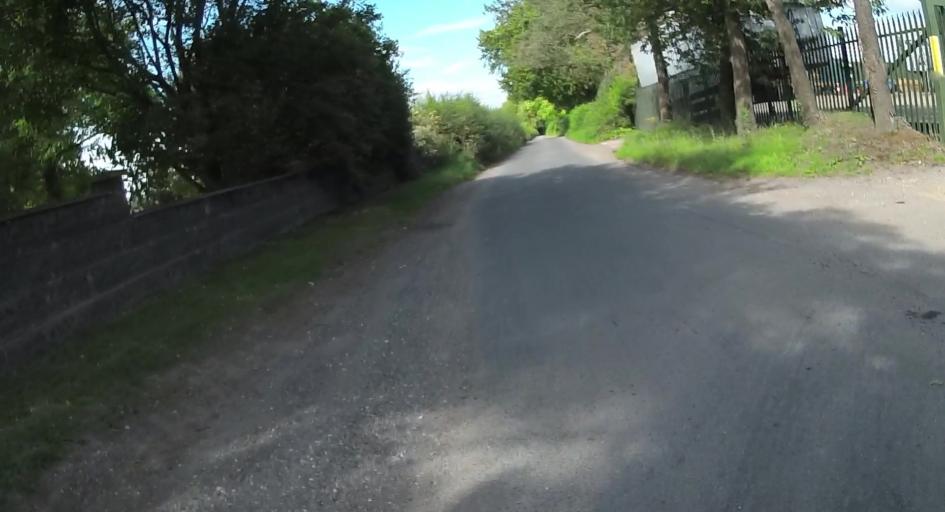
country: GB
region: England
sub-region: Hampshire
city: Overton
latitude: 51.1938
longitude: -1.2474
